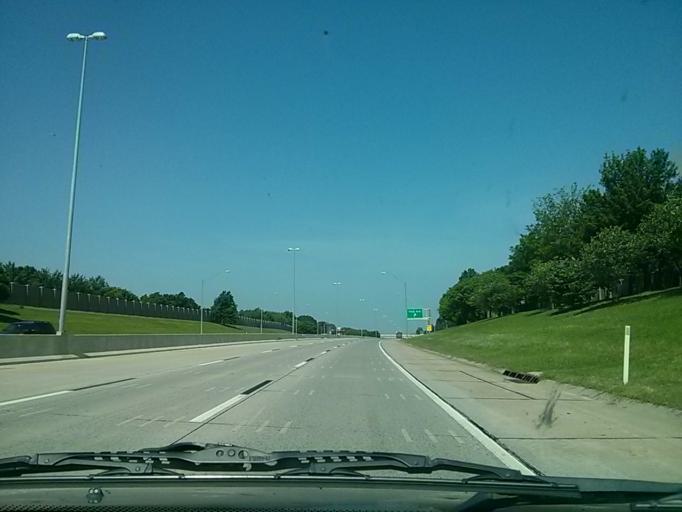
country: US
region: Oklahoma
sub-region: Tulsa County
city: Jenks
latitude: 36.0255
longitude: -95.9139
